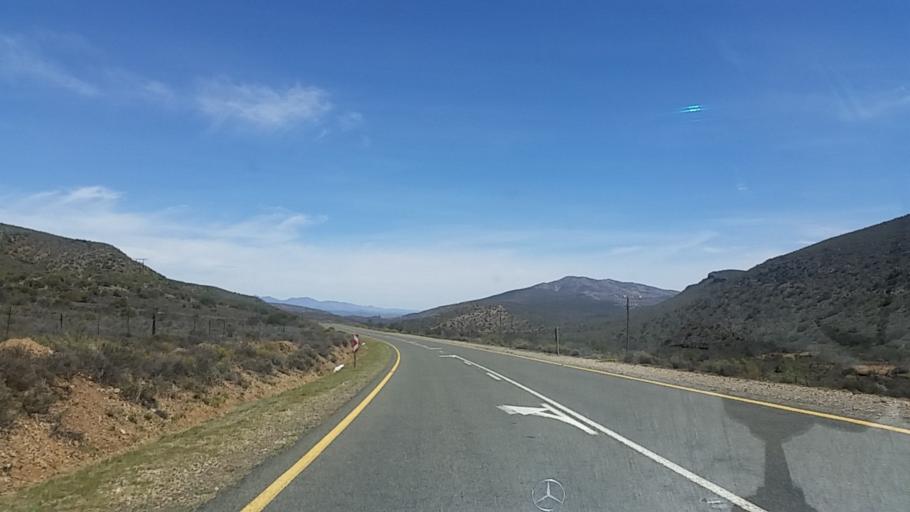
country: ZA
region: Eastern Cape
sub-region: Cacadu District Municipality
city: Willowmore
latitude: -33.3781
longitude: 23.4142
